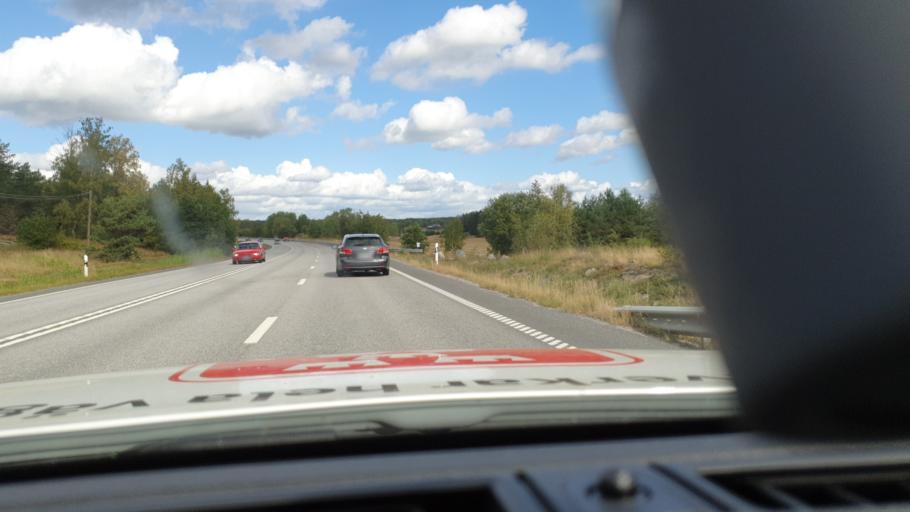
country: SE
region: Stockholm
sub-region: Osterakers Kommun
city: Akersberga
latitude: 59.4414
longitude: 18.2222
